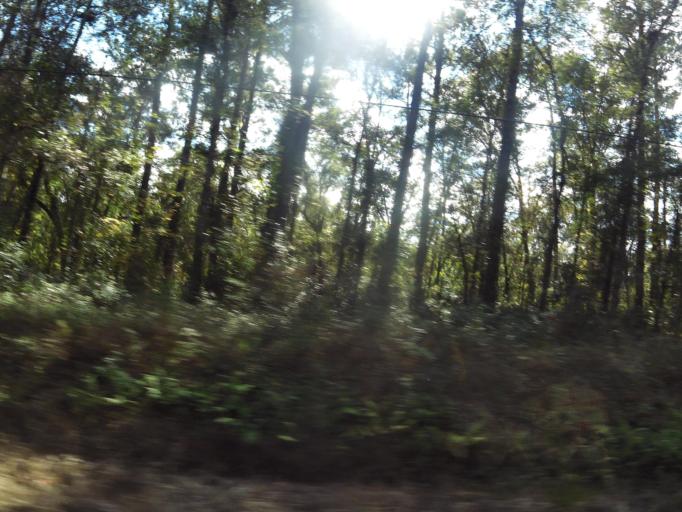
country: US
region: Florida
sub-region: Clay County
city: Middleburg
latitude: 30.1205
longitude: -81.9423
